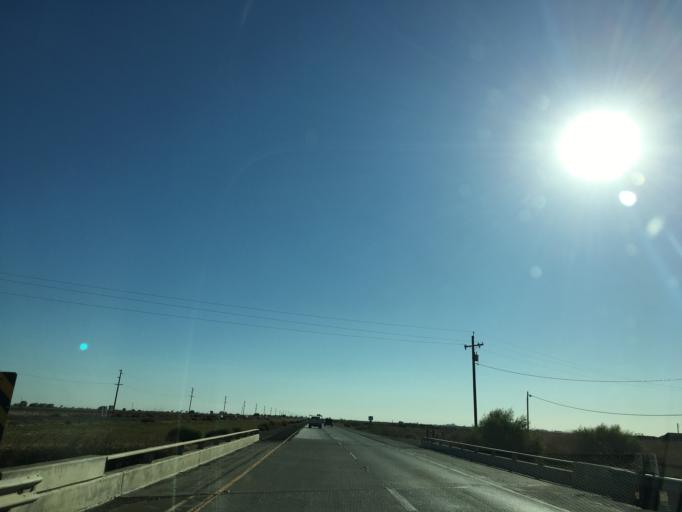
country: US
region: California
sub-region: Merced County
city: Los Banos
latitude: 37.0556
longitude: -120.7873
